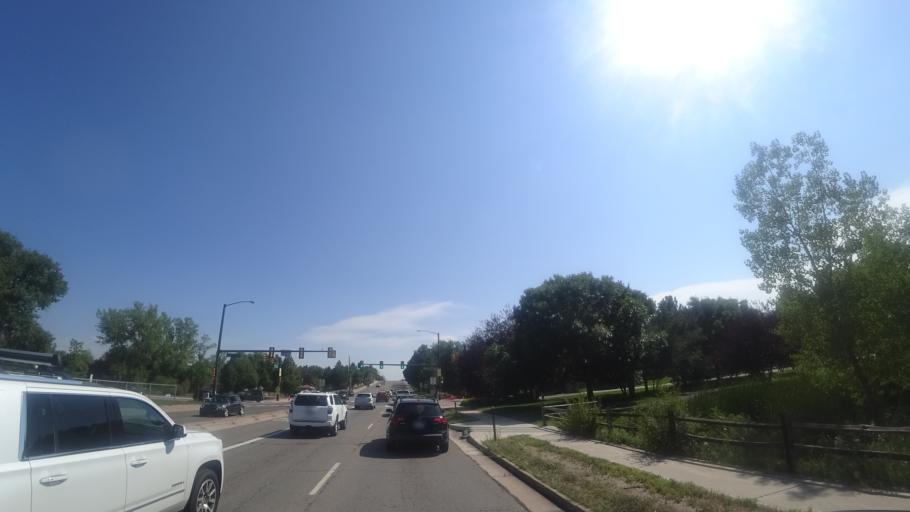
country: US
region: Colorado
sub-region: Arapahoe County
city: Cherry Hills Village
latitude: 39.6381
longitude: -104.9598
